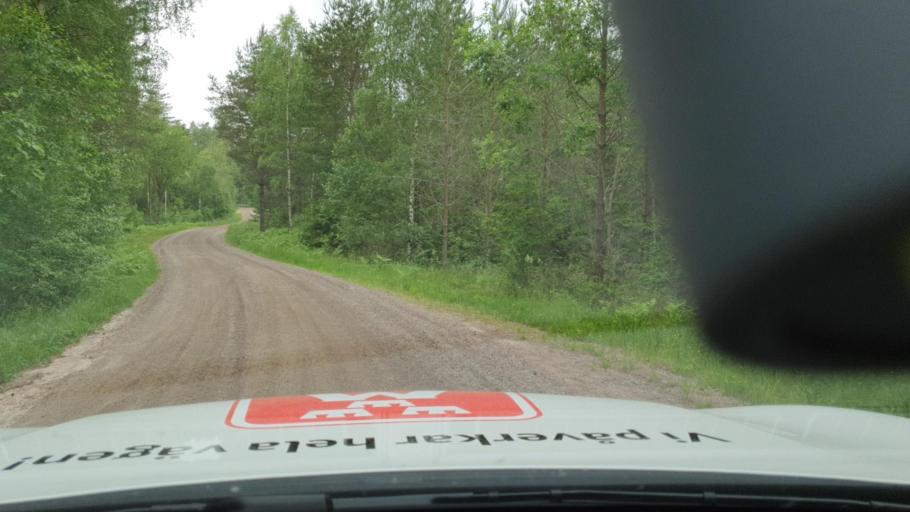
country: SE
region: Vaestra Goetaland
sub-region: Hjo Kommun
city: Hjo
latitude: 58.3391
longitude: 14.2735
